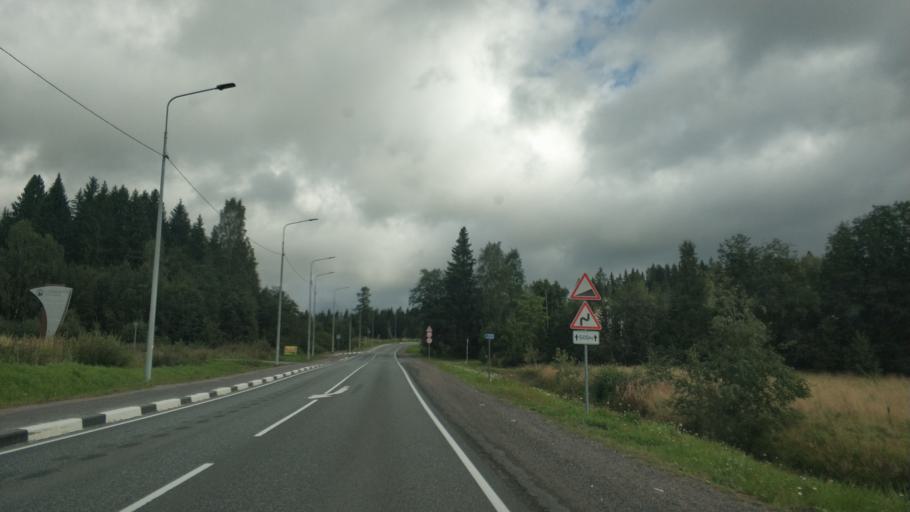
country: RU
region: Republic of Karelia
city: Khelyulya
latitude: 61.7655
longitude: 30.6551
